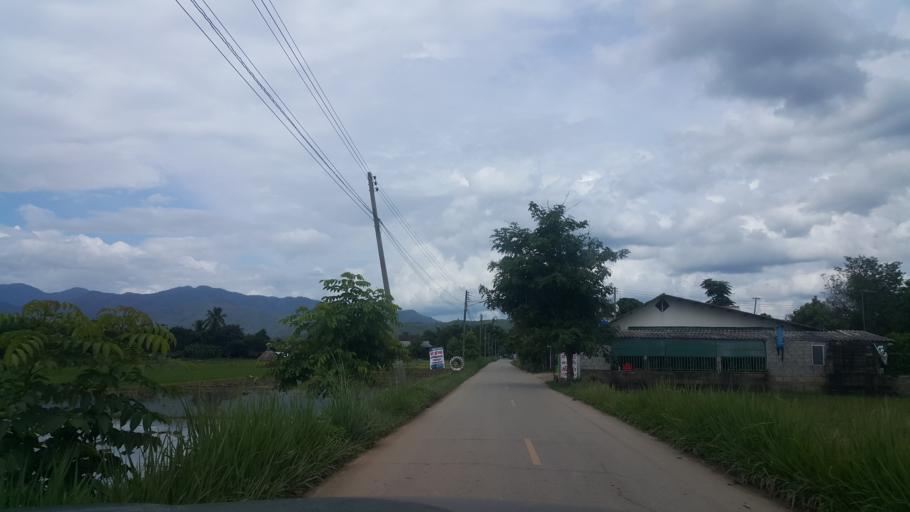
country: TH
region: Chiang Mai
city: Mae Taeng
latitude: 19.1816
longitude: 98.9872
